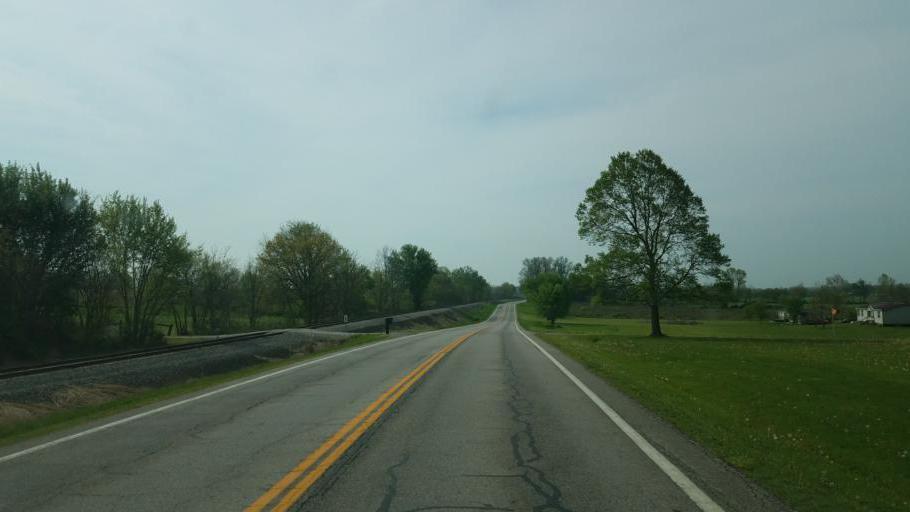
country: US
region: Ohio
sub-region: Licking County
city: Utica
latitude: 40.2896
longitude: -82.4503
